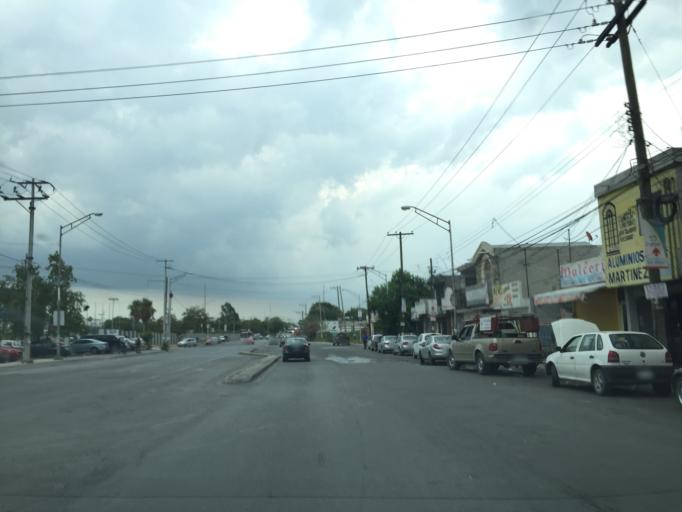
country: MX
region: Nuevo Leon
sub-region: Juarez
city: Valle de Juarez
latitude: 25.6633
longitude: -100.1765
